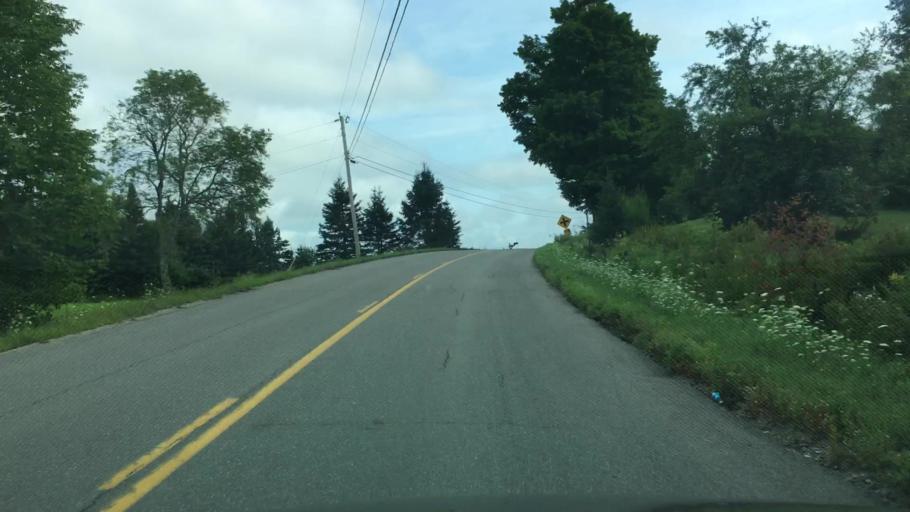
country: US
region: Maine
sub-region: Waldo County
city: Winterport
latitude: 44.6815
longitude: -68.8685
